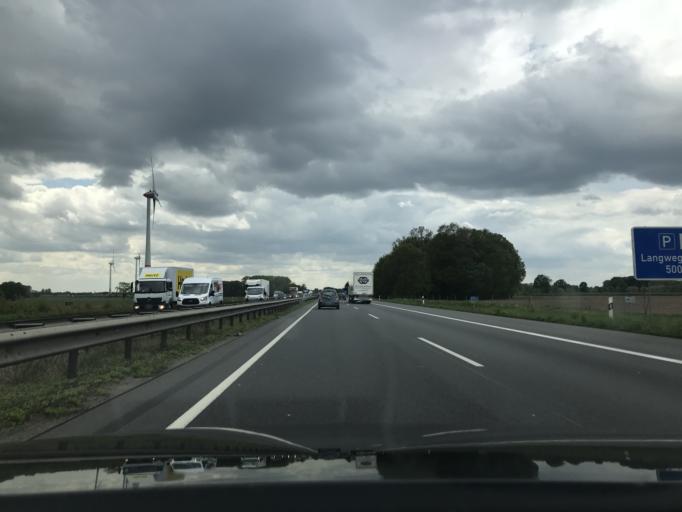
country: DE
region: Lower Saxony
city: Holdorf
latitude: 52.6212
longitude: 8.1337
